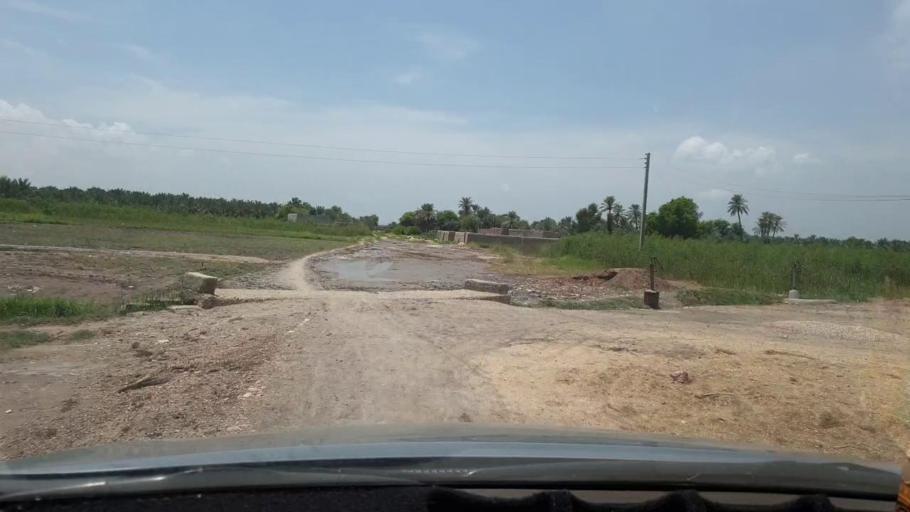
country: PK
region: Sindh
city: Khairpur
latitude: 27.4535
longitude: 68.7786
